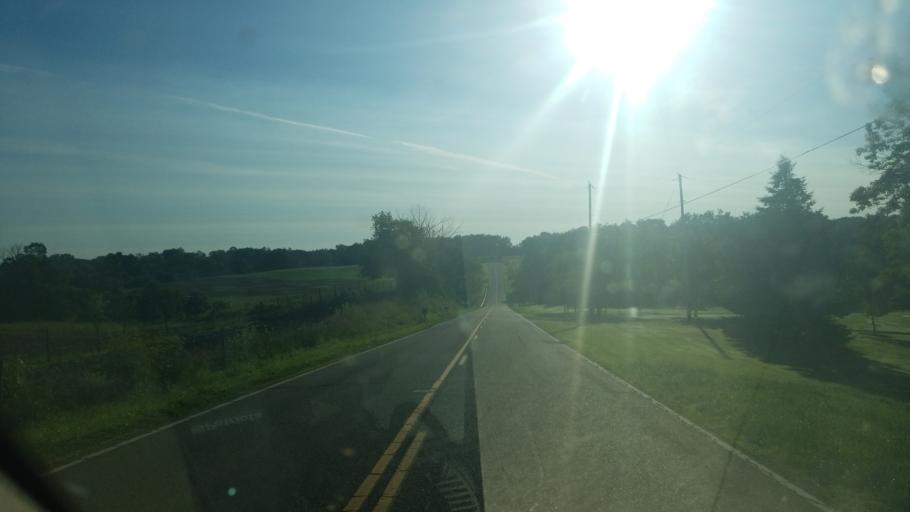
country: US
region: Ohio
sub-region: Columbiana County
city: Salem
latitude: 40.8749
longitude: -80.9211
